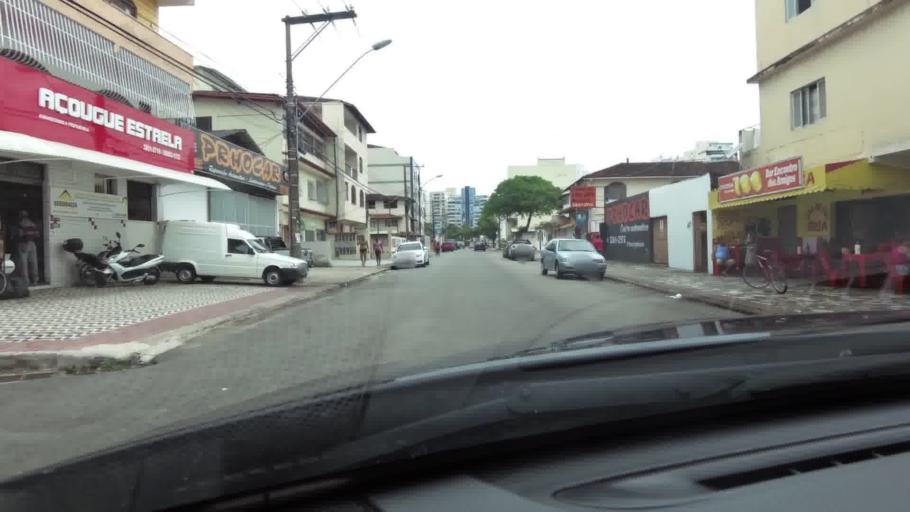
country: BR
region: Espirito Santo
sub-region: Guarapari
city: Guarapari
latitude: -20.6622
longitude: -40.5007
